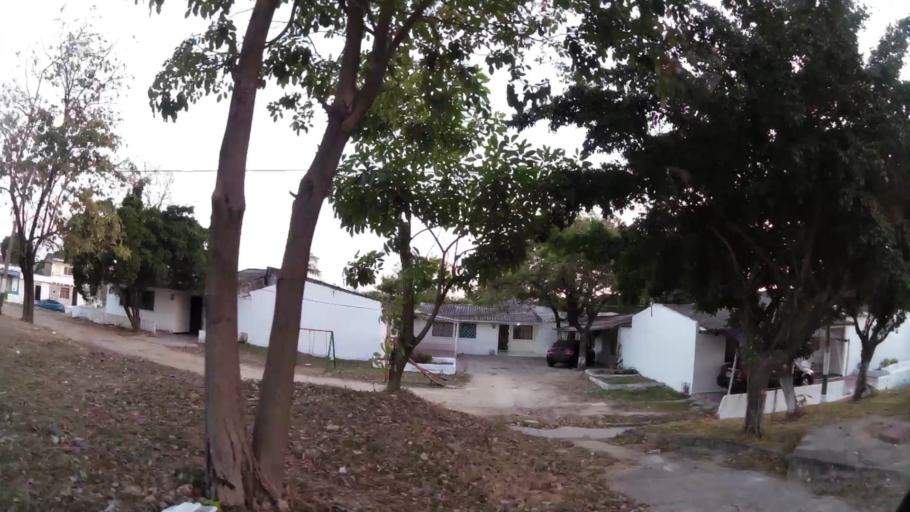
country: CO
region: Bolivar
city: Cartagena
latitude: 10.3906
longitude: -75.4890
